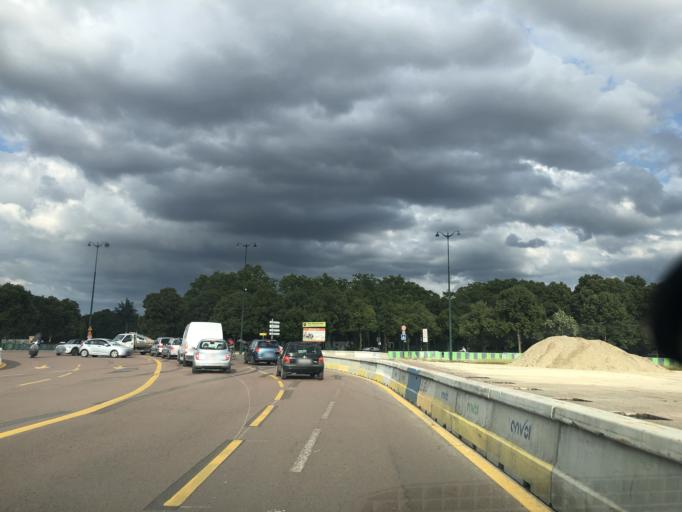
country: FR
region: Ile-de-France
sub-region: Departement du Val-de-Marne
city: Vincennes
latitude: 48.8403
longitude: 2.4356
